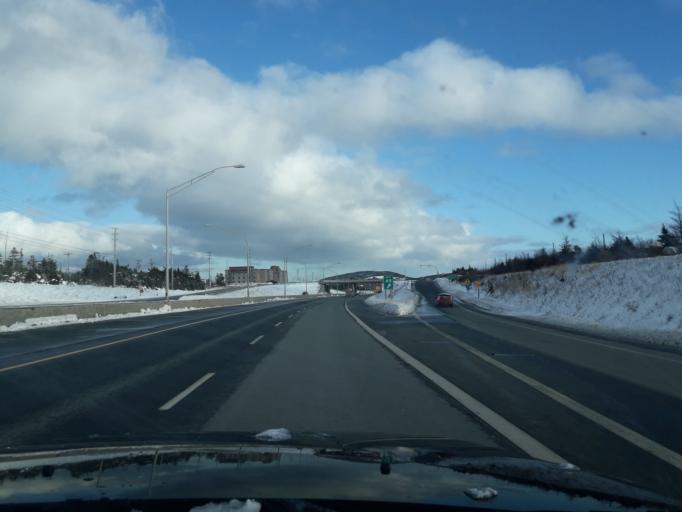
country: CA
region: Newfoundland and Labrador
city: St. John's
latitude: 47.6126
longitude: -52.7150
